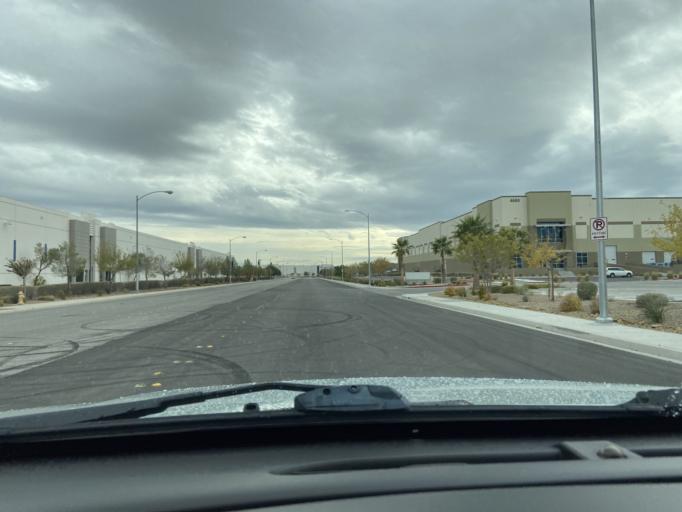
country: US
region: Nevada
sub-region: Clark County
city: North Las Vegas
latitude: 36.2460
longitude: -115.1079
